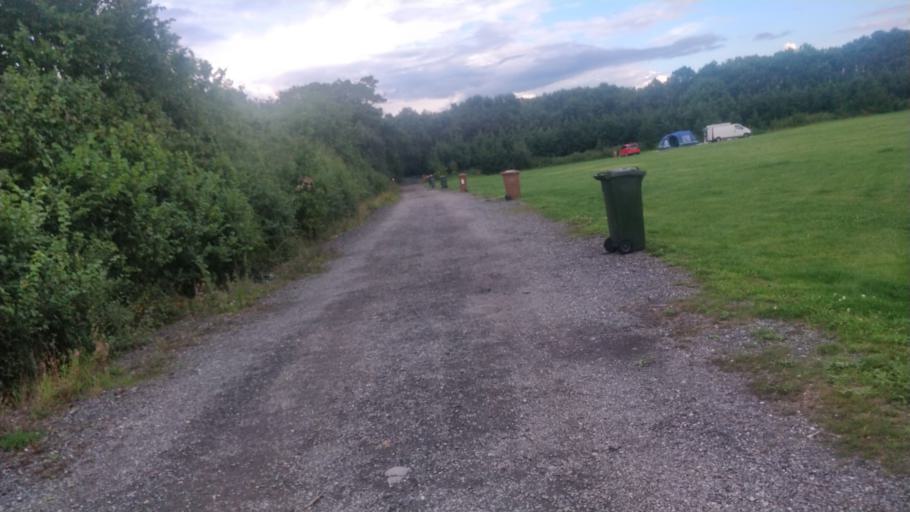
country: GB
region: Wales
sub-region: Wrexham
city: Rossett
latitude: 53.1468
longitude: -2.9354
